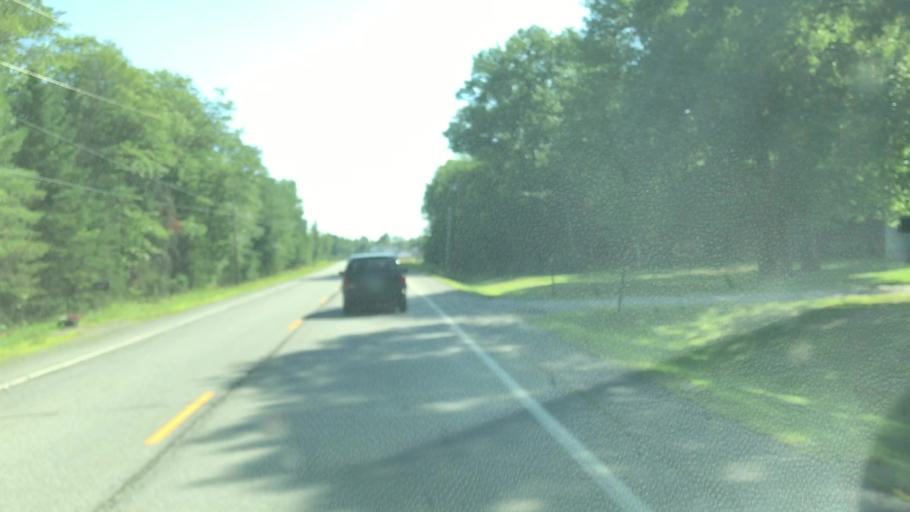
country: US
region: Maine
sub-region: Penobscot County
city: Enfield
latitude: 45.3011
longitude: -68.6166
